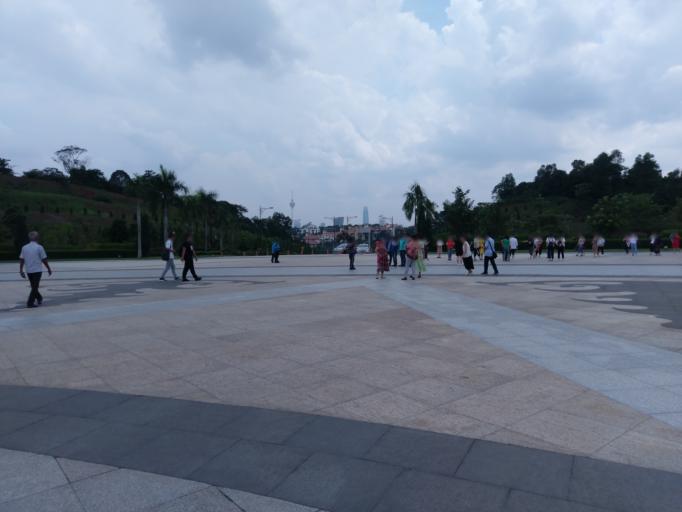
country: MY
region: Kuala Lumpur
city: Kuala Lumpur
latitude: 3.1597
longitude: 101.6676
